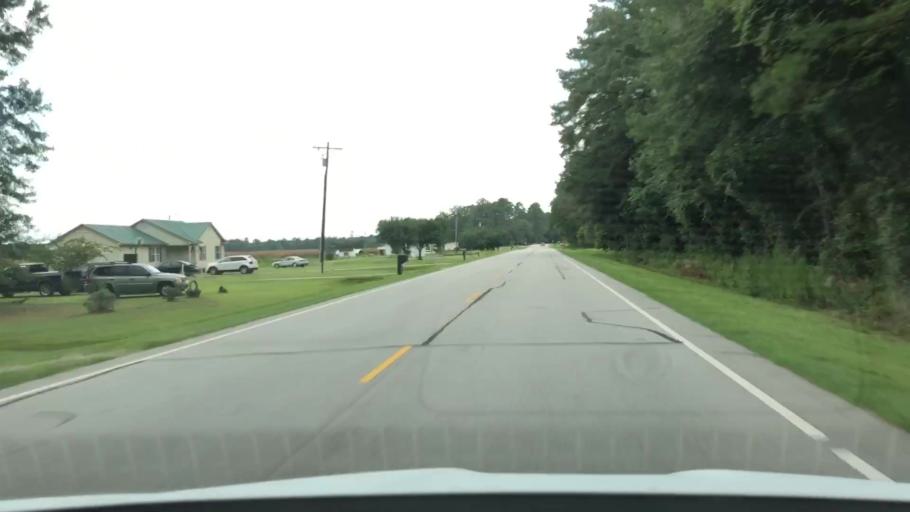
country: US
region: North Carolina
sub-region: Lenoir County
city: Kinston
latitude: 35.1174
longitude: -77.5134
